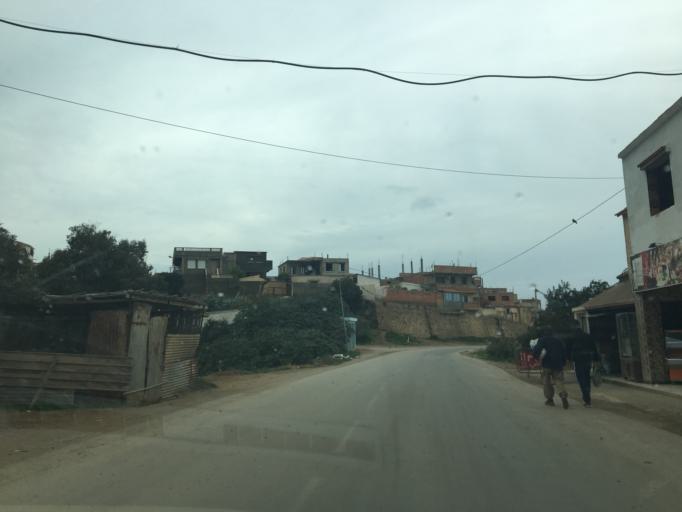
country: DZ
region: Tipaza
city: Tipasa
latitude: 36.6407
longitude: 2.3624
